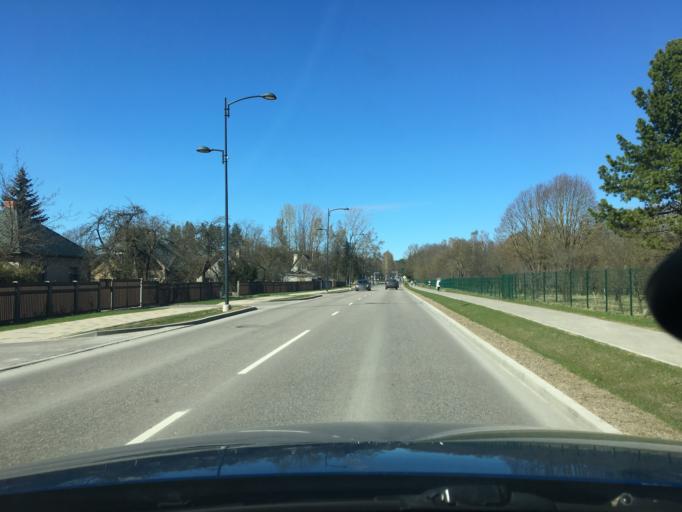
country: LV
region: Salaspils
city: Salaspils
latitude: 56.8656
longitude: 24.3517
